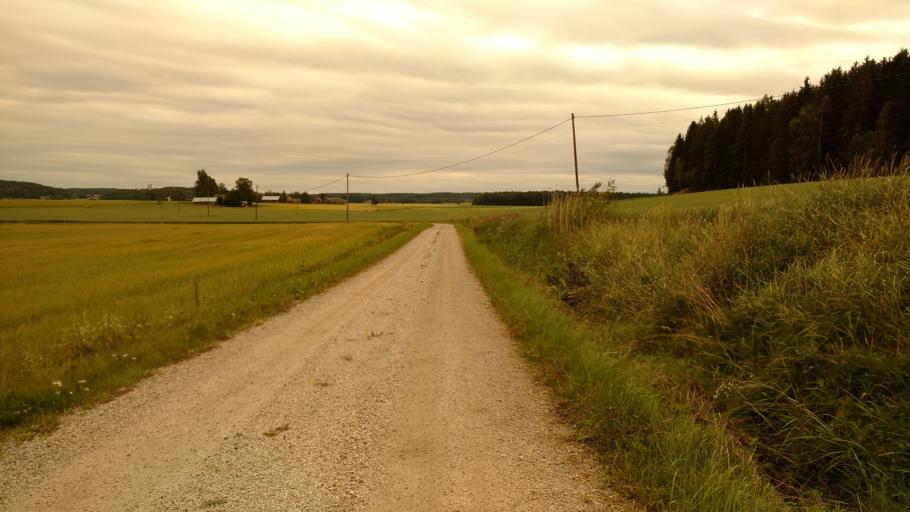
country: FI
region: Varsinais-Suomi
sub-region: Turku
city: Paimio
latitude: 60.4170
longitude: 22.8343
